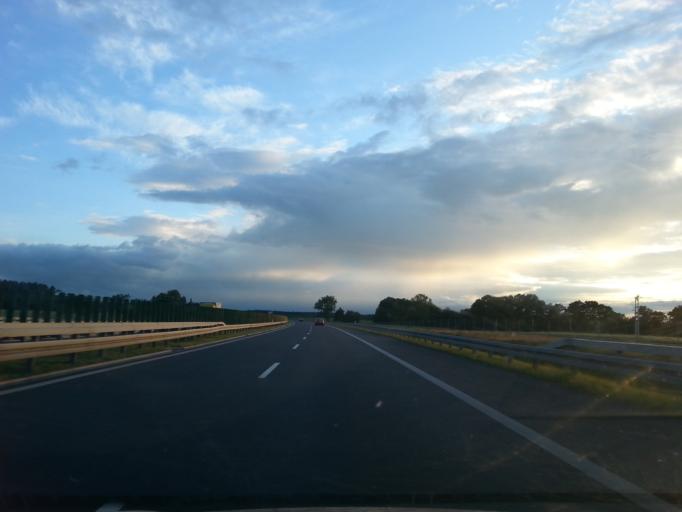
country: PL
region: Lower Silesian Voivodeship
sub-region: Powiat olesnicki
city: Miedzyborz
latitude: 51.3056
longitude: 17.6075
